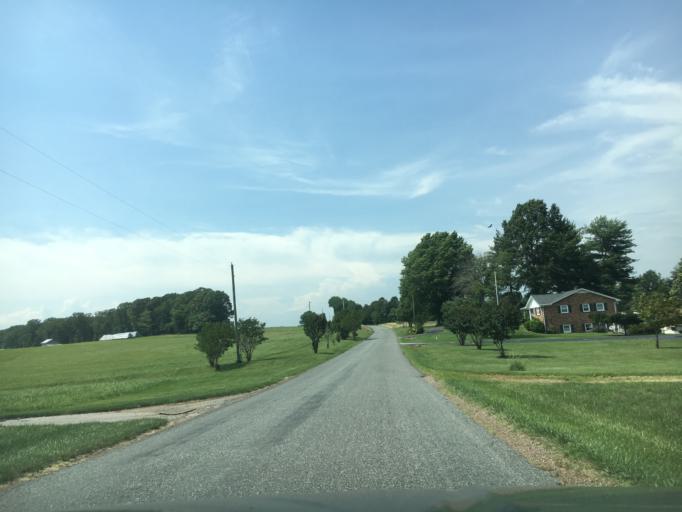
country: US
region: Virginia
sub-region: Pittsylvania County
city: Gretna
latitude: 36.9136
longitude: -79.4210
